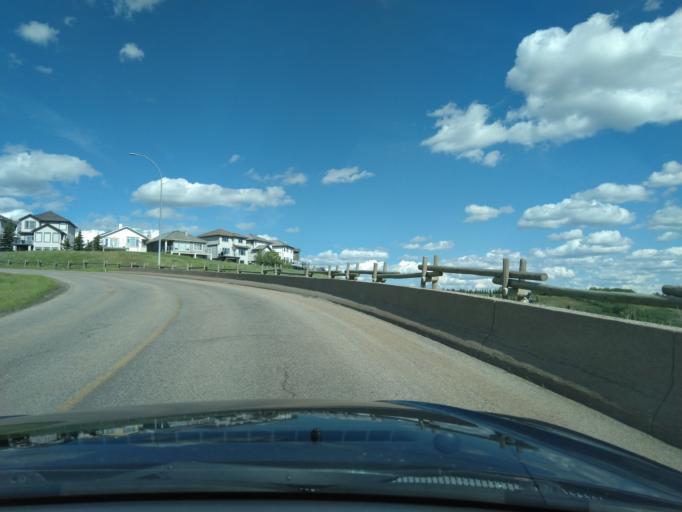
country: CA
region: Alberta
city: Cochrane
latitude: 51.1947
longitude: -114.4241
